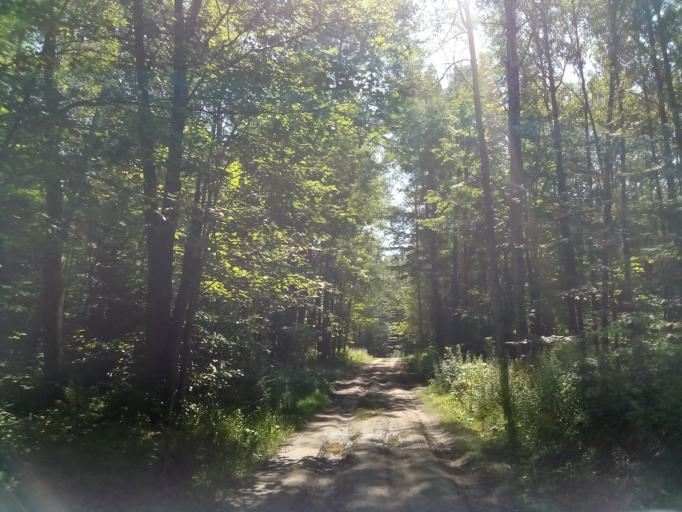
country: US
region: Wisconsin
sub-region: Forest County
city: Crandon
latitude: 45.3646
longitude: -88.5215
